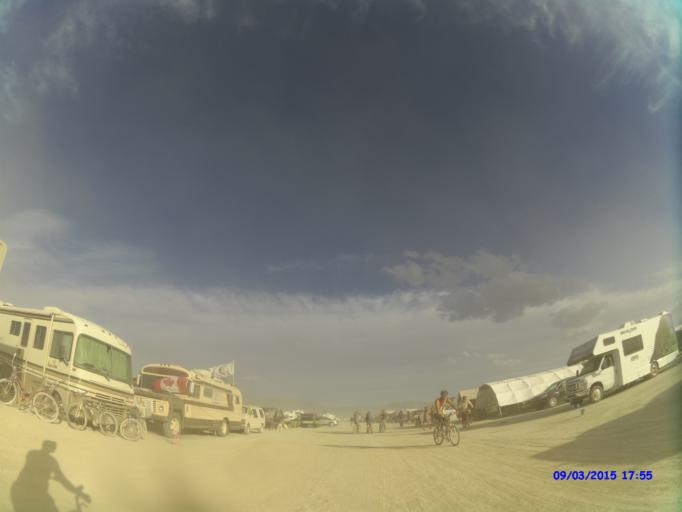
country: US
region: Nevada
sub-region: Pershing County
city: Lovelock
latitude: 40.7771
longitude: -119.2180
